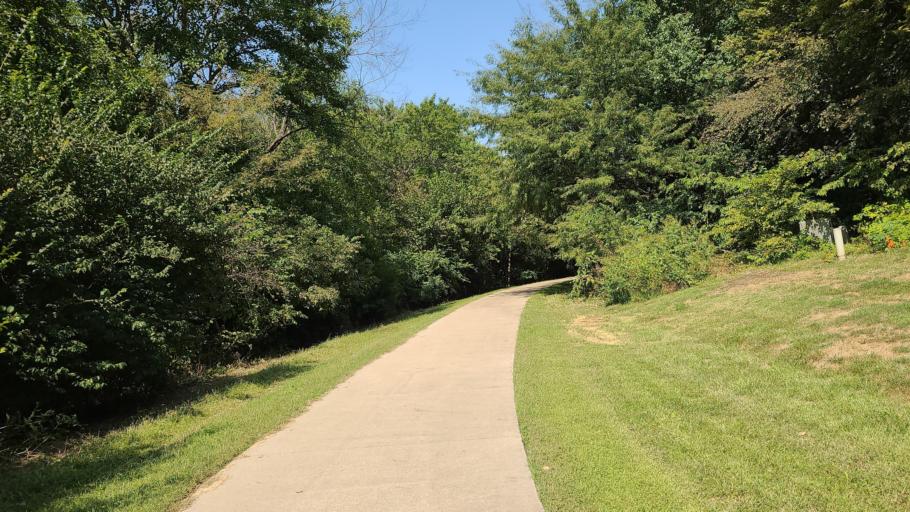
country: US
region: Kansas
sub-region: Douglas County
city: Lawrence
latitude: 38.9627
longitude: -95.3238
